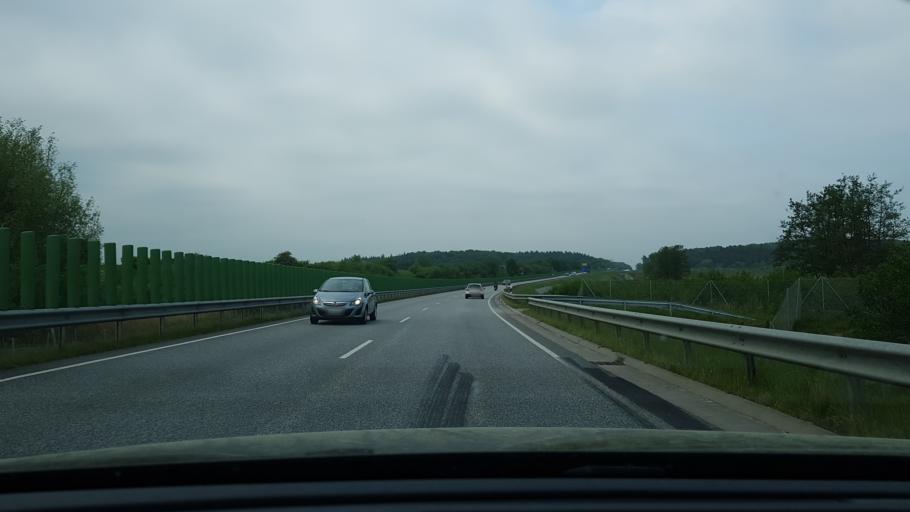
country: DE
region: Schleswig-Holstein
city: Gross Sarau
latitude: 53.7778
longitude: 10.7080
